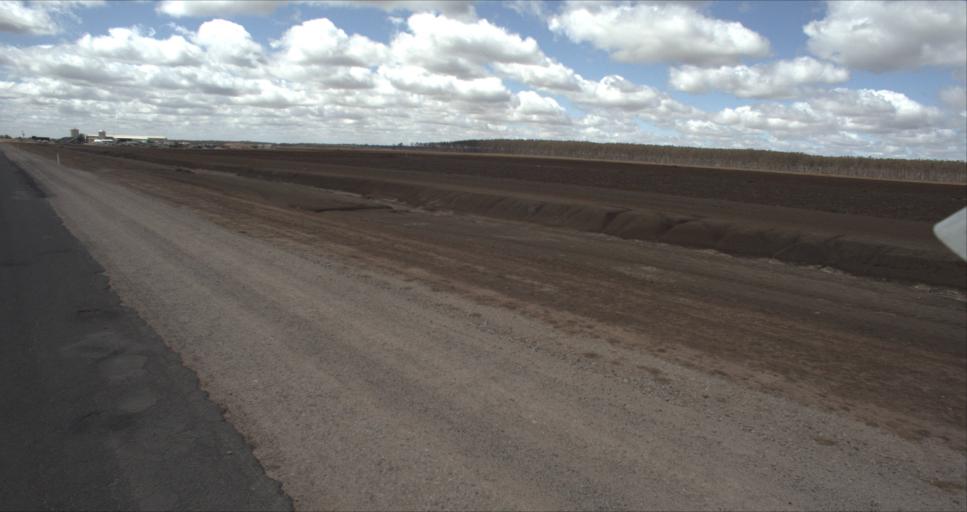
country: AU
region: New South Wales
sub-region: Murrumbidgee Shire
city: Darlington Point
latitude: -34.5753
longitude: 146.1724
